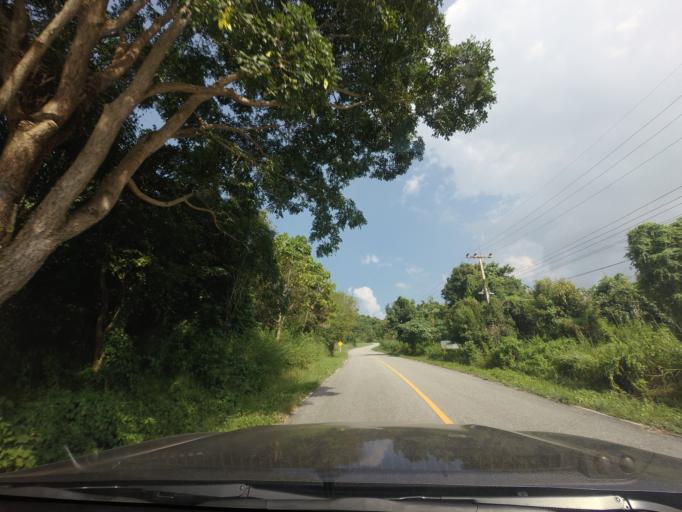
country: TH
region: Phitsanulok
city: Nakhon Thai
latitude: 17.0210
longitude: 100.9687
